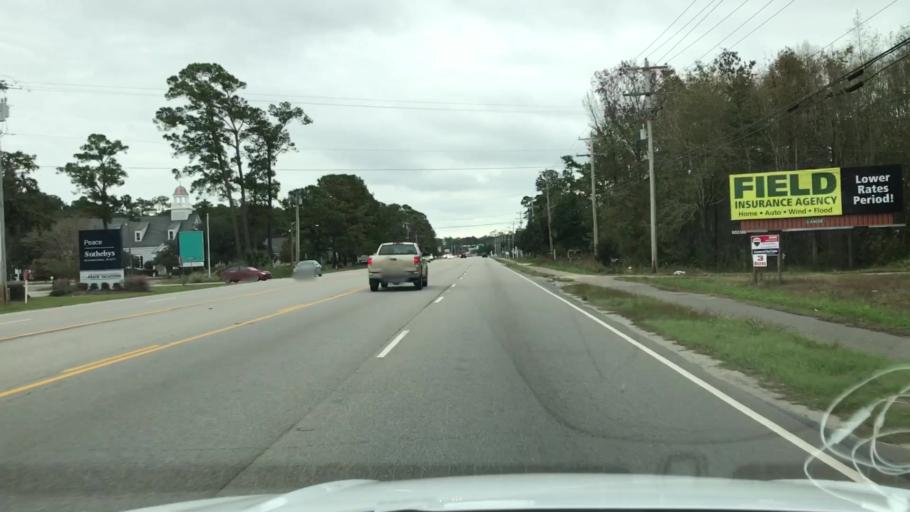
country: US
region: South Carolina
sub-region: Georgetown County
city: Murrells Inlet
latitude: 33.4341
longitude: -79.1366
